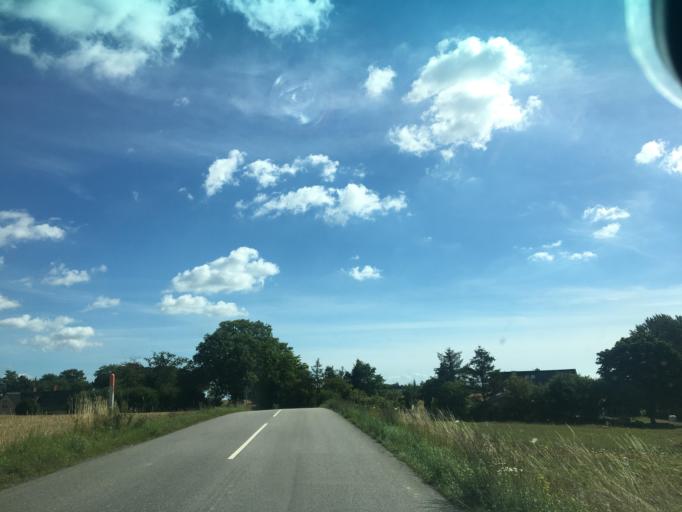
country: DK
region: Zealand
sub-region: Greve Kommune
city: Tune
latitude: 55.5668
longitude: 12.1974
